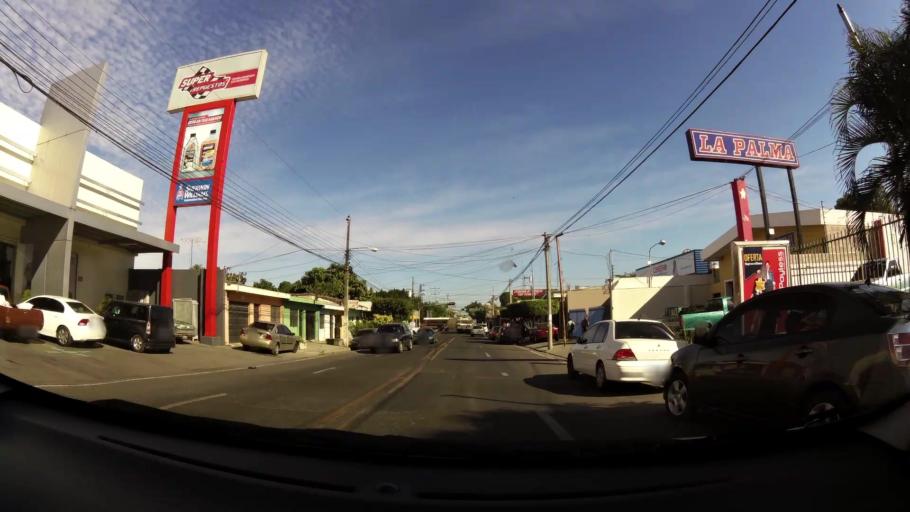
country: SV
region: Santa Ana
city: Santa Ana
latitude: 13.9844
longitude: -89.5671
